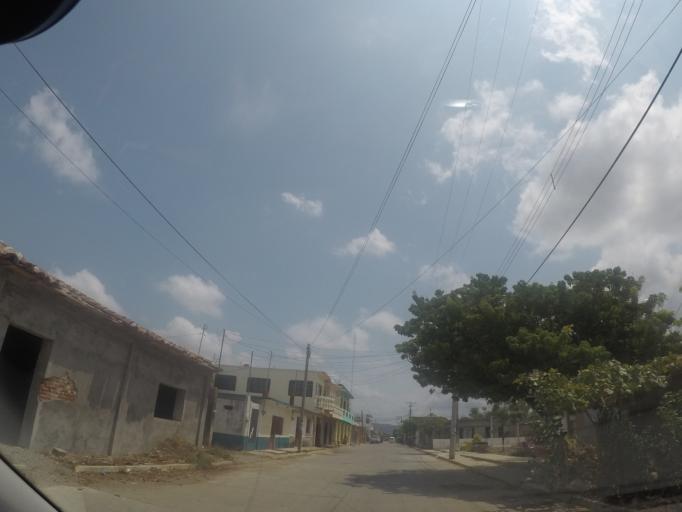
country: MX
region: Oaxaca
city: El Espinal
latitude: 16.5514
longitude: -94.9472
